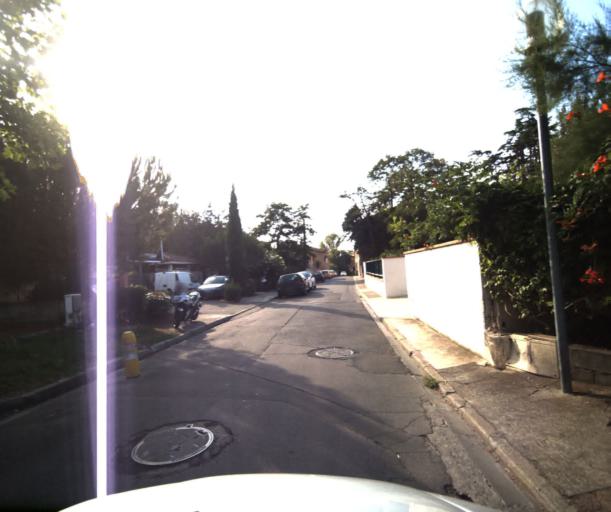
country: FR
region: Midi-Pyrenees
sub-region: Departement de la Haute-Garonne
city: Muret
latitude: 43.4573
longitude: 1.3307
